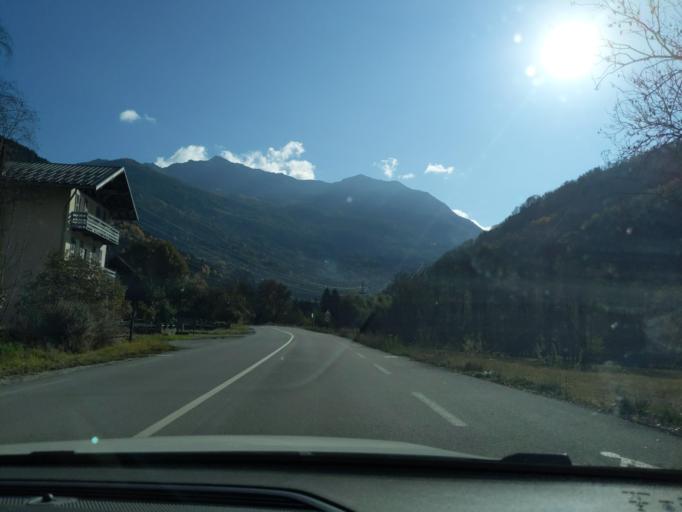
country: FR
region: Rhone-Alpes
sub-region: Departement de la Savoie
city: Seez
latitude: 45.6041
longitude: 6.8577
